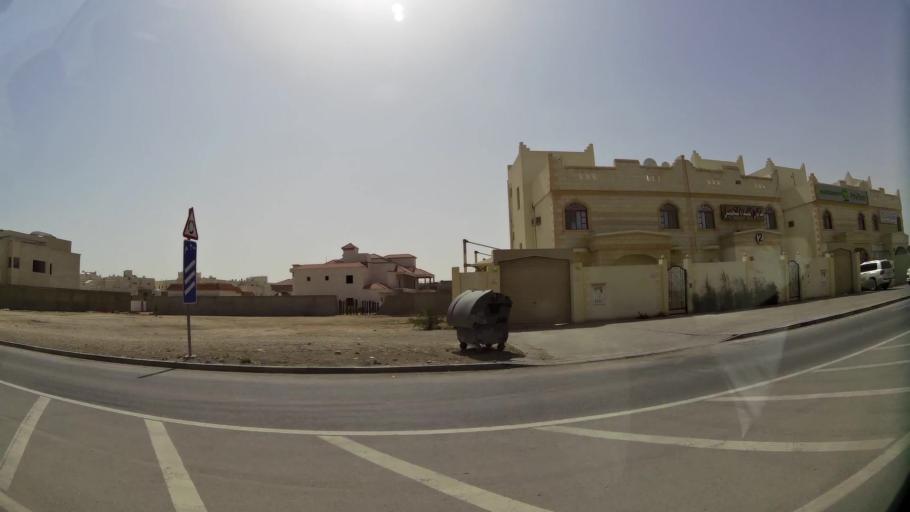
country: QA
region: Baladiyat Umm Salal
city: Umm Salal Muhammad
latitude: 25.3972
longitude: 51.4255
